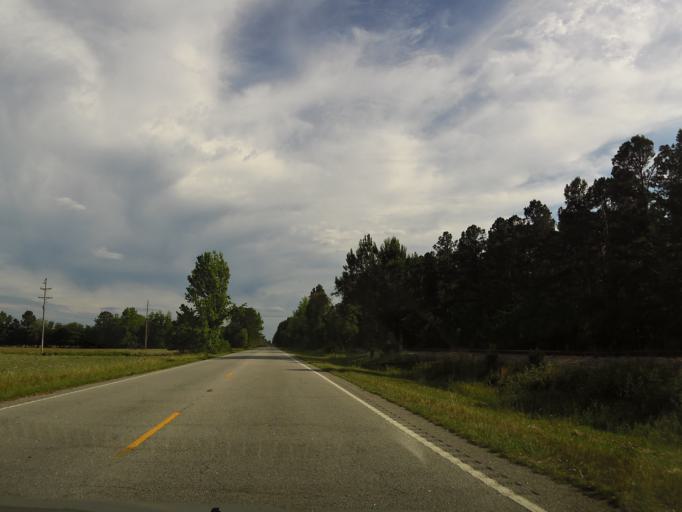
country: US
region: South Carolina
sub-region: Hampton County
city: Estill
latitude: 32.8391
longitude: -81.2393
